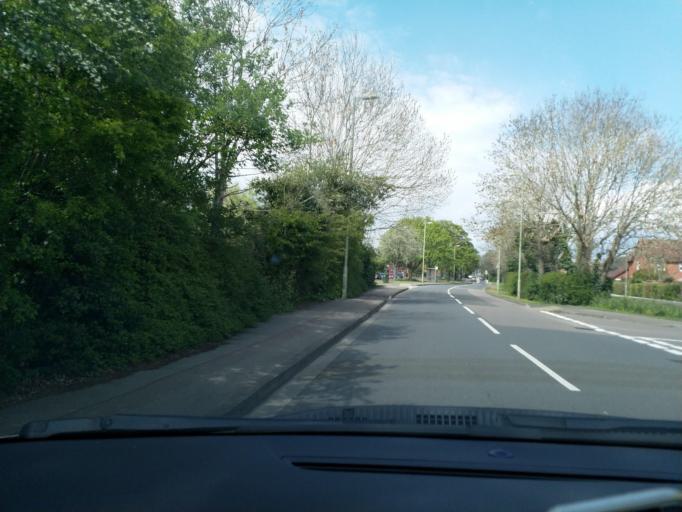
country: GB
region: England
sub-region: Suffolk
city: Woodbridge
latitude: 52.0684
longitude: 1.3209
